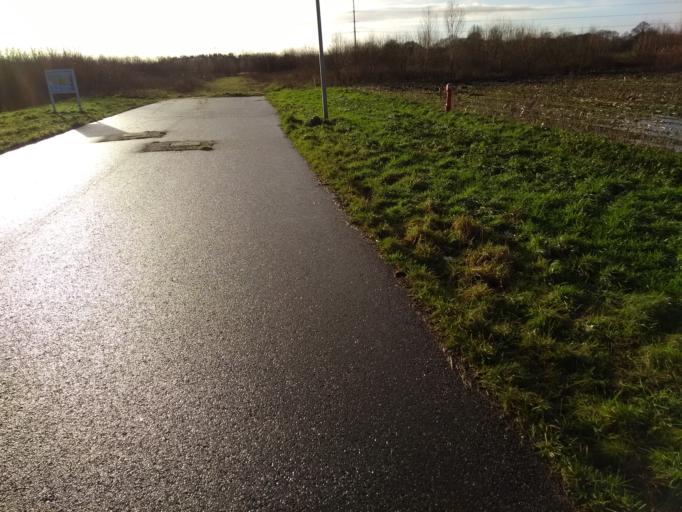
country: NL
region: Overijssel
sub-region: Gemeente Wierden
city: Wierden
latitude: 52.3843
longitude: 6.6022
